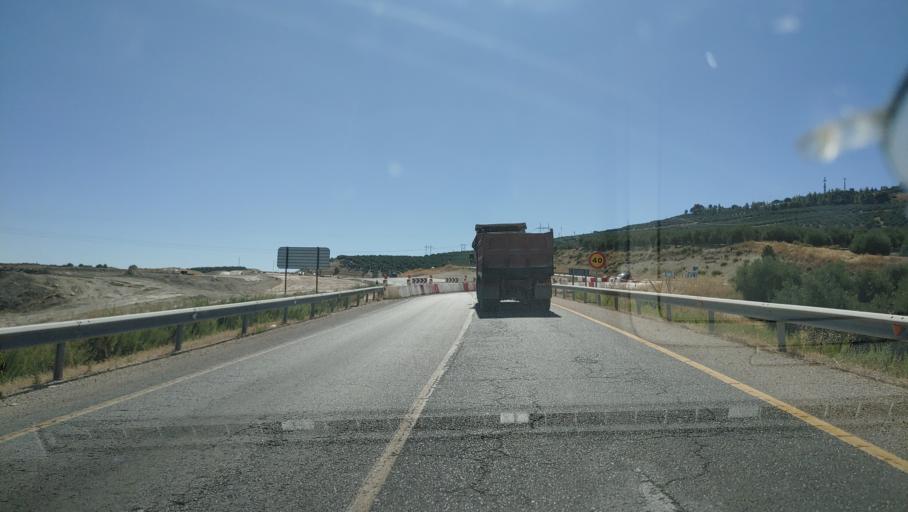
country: ES
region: Andalusia
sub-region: Provincia de Jaen
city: Villanueva del Arzobispo
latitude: 38.1542
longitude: -3.0157
